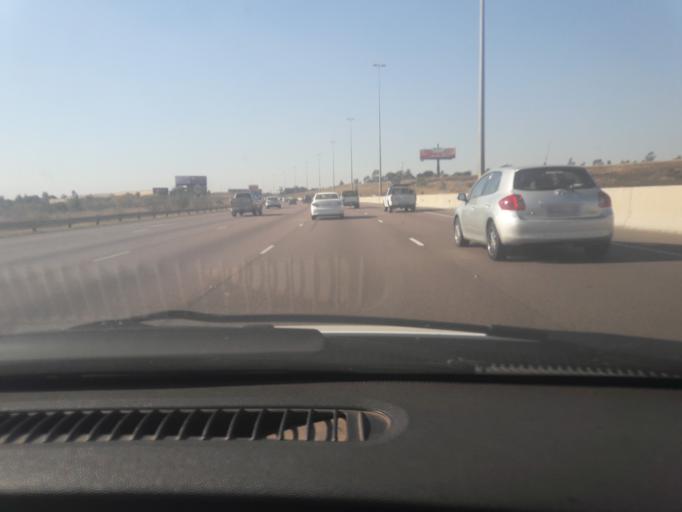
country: ZA
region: Gauteng
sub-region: City of Tshwane Metropolitan Municipality
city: Centurion
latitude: -25.8563
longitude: 28.2238
